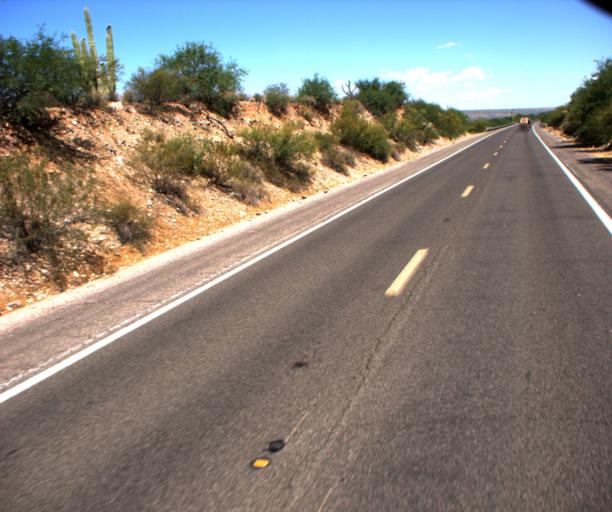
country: US
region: Arizona
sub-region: Pinal County
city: Mammoth
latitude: 32.8175
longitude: -110.6910
